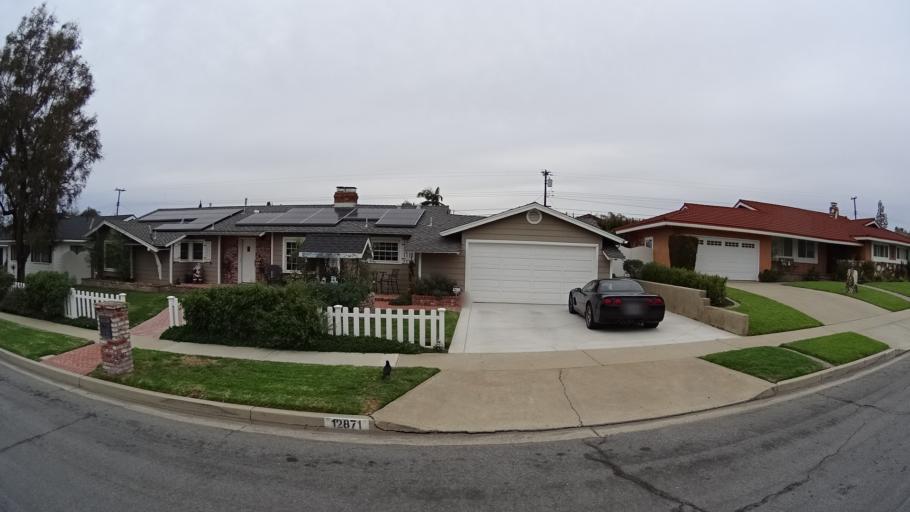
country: US
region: California
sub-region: Orange County
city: North Tustin
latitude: 33.7433
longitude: -117.7994
